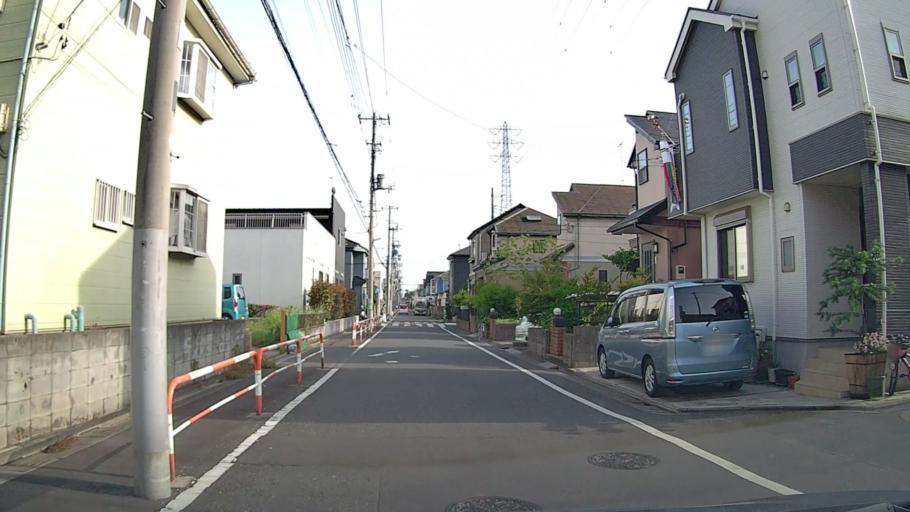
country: JP
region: Saitama
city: Soka
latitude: 35.7949
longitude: 139.7774
